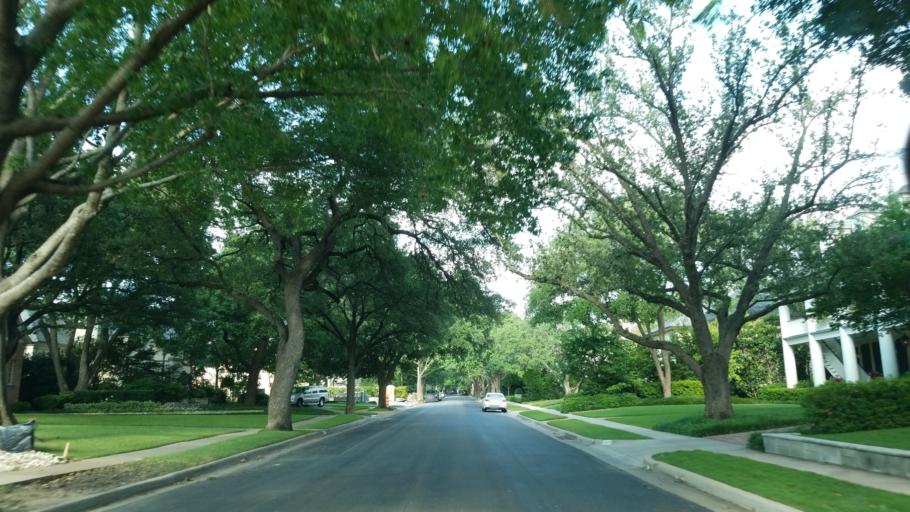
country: US
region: Texas
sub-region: Dallas County
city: Highland Park
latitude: 32.8377
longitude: -96.7972
